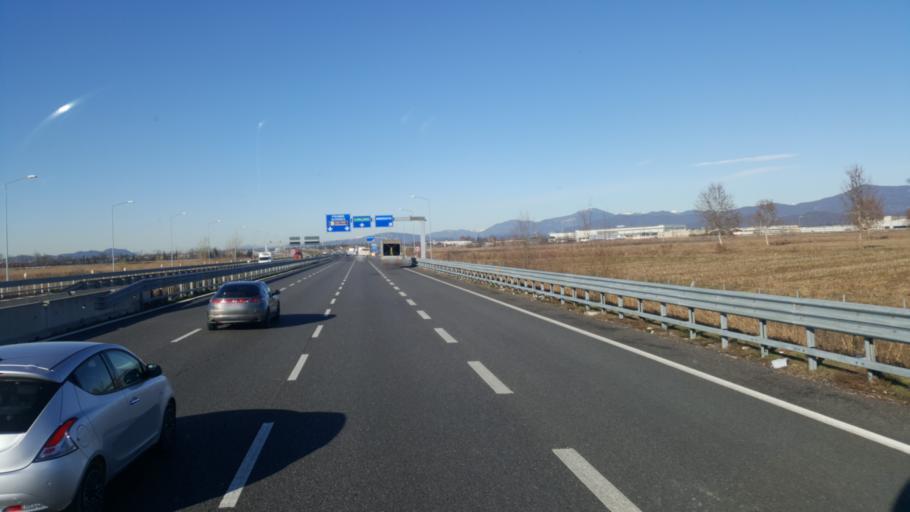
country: IT
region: Lombardy
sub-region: Provincia di Brescia
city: Roncadelle
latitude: 45.5424
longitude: 10.1433
